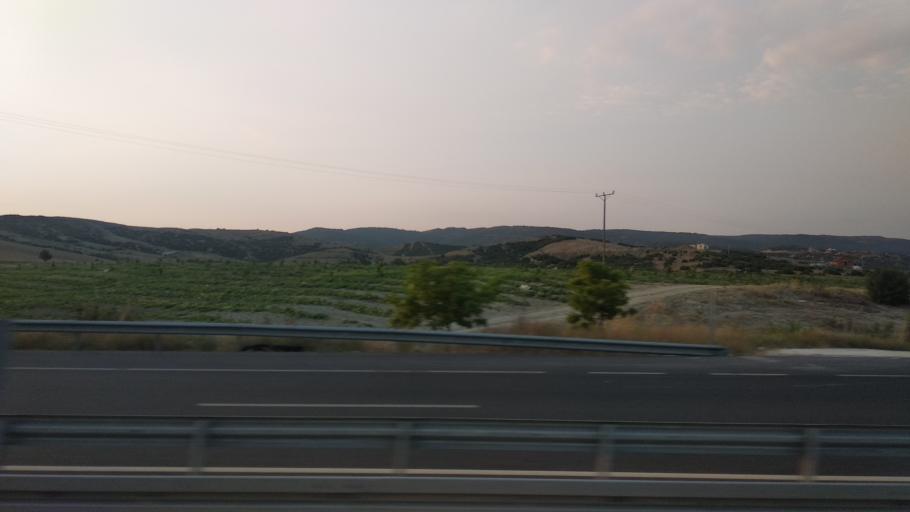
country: TR
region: Manisa
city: Selendi
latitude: 38.6233
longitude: 28.9270
